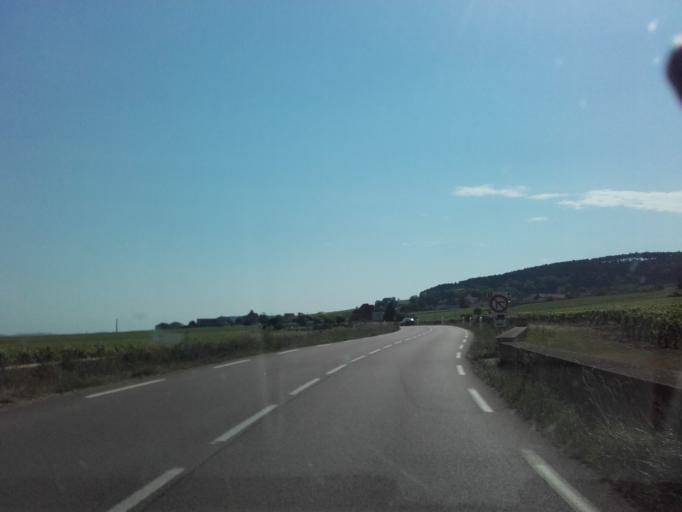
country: FR
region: Bourgogne
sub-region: Departement de la Cote-d'Or
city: Meursault
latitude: 47.0040
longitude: 4.7914
